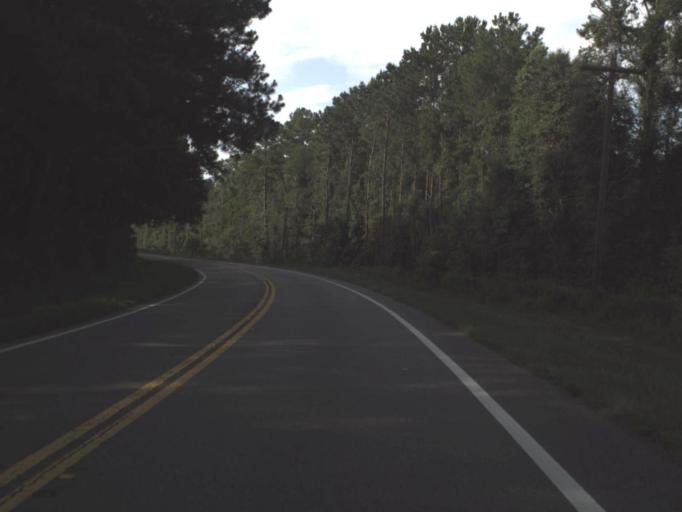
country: US
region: Florida
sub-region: Madison County
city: Madison
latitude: 30.4578
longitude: -83.6319
